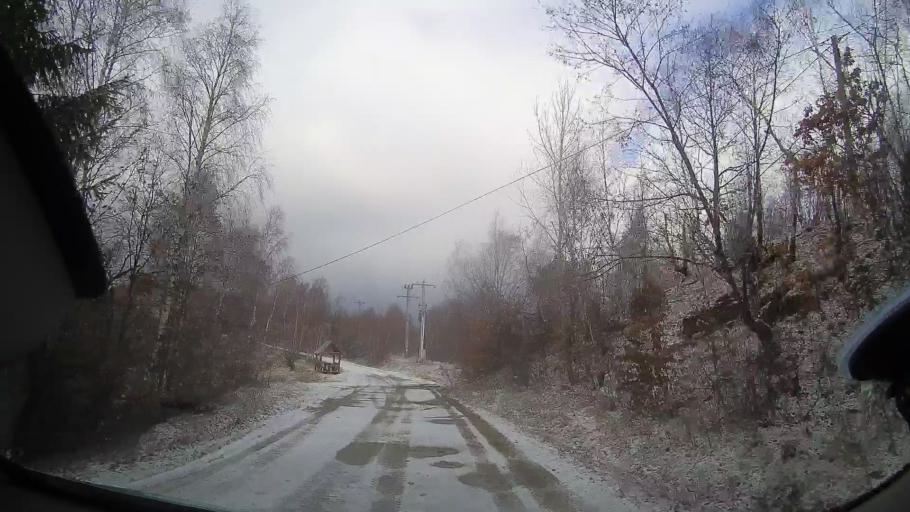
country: RO
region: Cluj
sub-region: Comuna Valea Ierii
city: Valea Ierii
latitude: 46.6553
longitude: 23.3496
